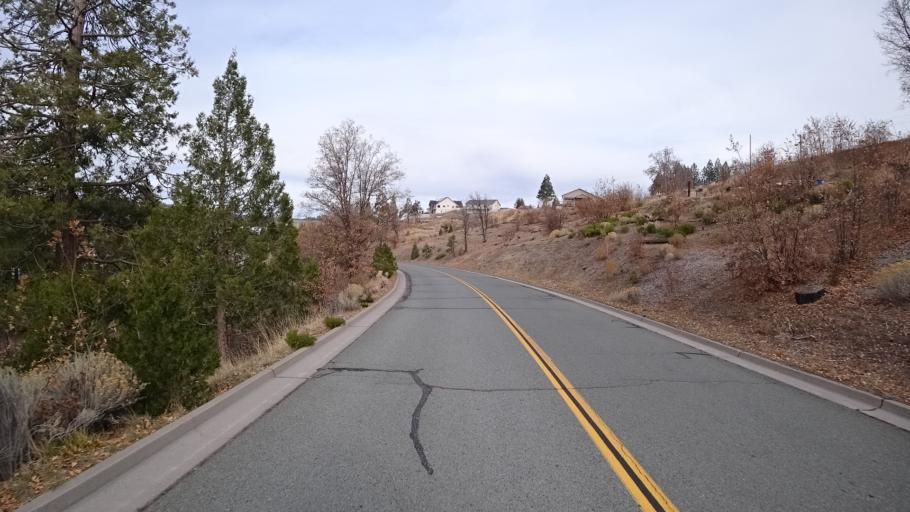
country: US
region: California
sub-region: Siskiyou County
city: Weed
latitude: 41.4273
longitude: -122.3820
